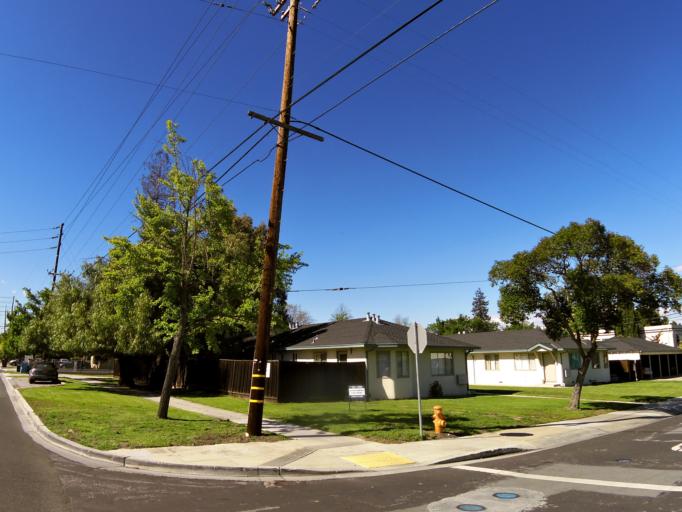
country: US
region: California
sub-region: Santa Clara County
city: Palo Alto
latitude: 37.4239
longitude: -122.1328
